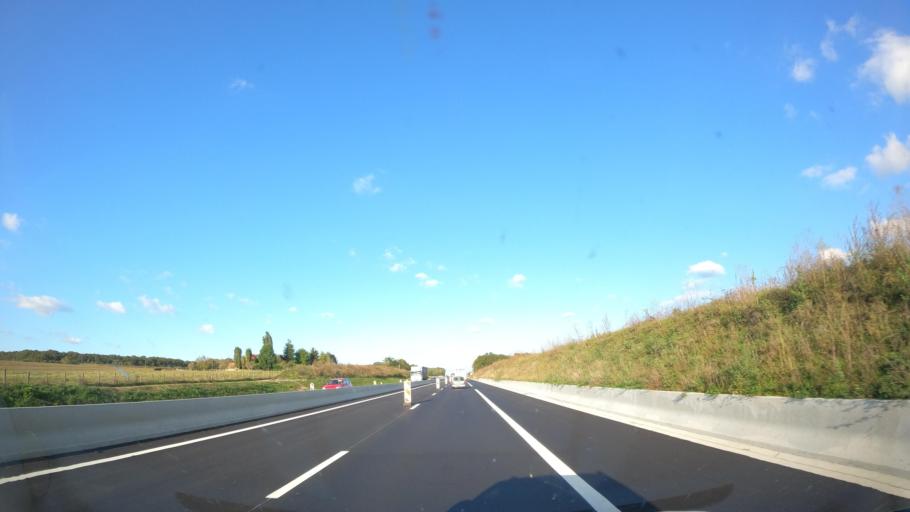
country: FR
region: Bourgogne
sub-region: Departement de Saone-et-Loire
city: Blanzy
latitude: 46.7052
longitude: 4.4183
